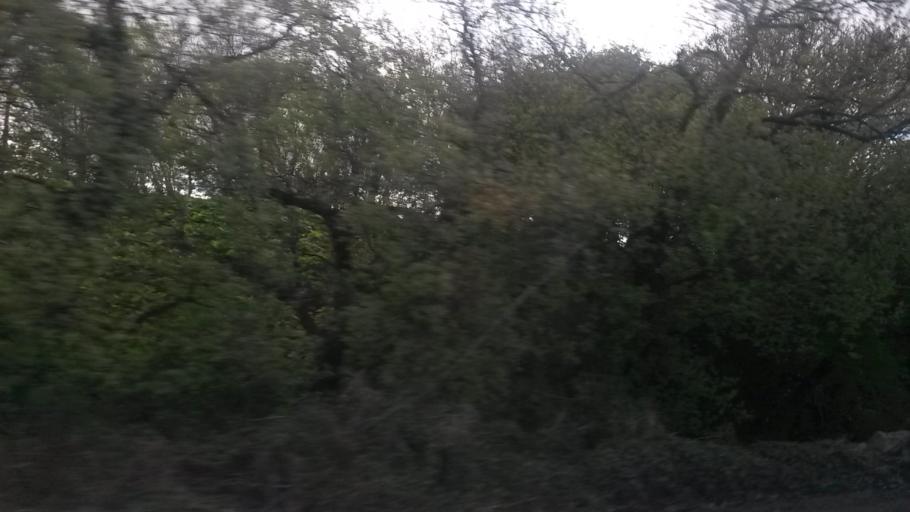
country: IE
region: Munster
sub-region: County Cork
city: Cobh
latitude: 51.8858
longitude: -8.3108
